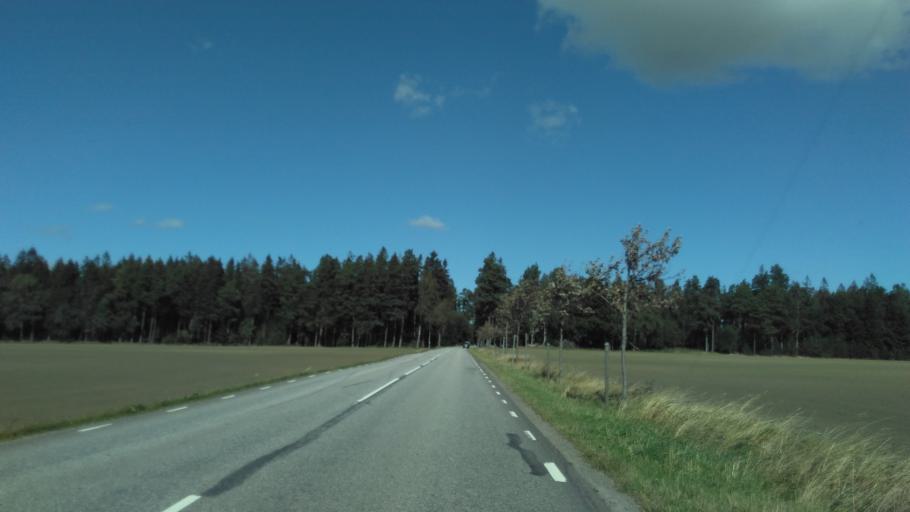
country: SE
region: Vaestra Goetaland
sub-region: Vara Kommun
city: Vara
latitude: 58.2313
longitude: 13.0029
